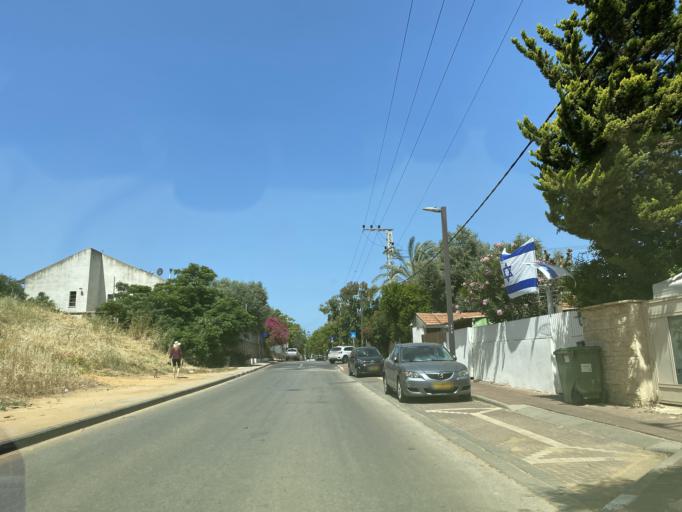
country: IL
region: Tel Aviv
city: Ramat HaSharon
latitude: 32.1535
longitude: 34.8368
